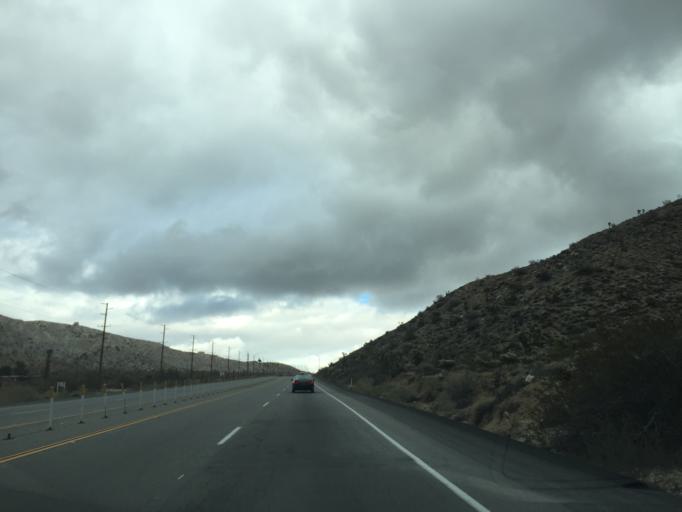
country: US
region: California
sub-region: San Bernardino County
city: Yucca Valley
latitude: 34.1022
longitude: -116.4953
